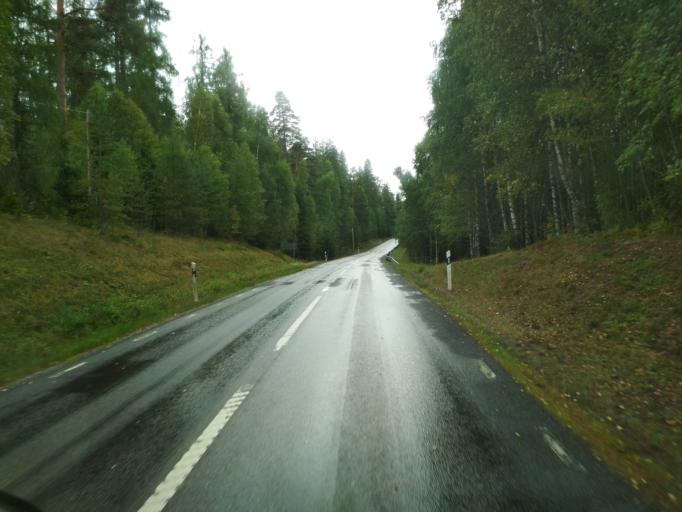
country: SE
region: Vaestmanland
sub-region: Surahammars Kommun
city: Surahammar
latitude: 59.7289
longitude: 16.2014
